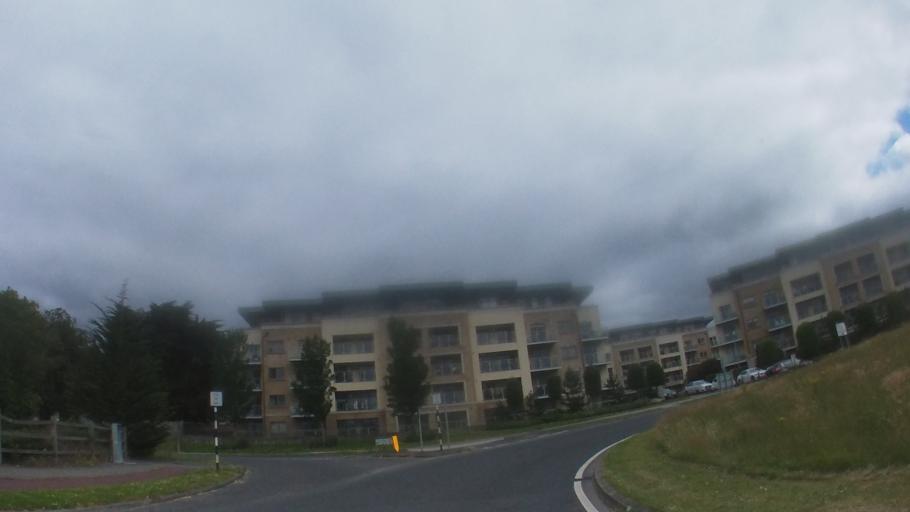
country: IE
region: Leinster
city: Foxrock
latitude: 53.2507
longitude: -6.1799
